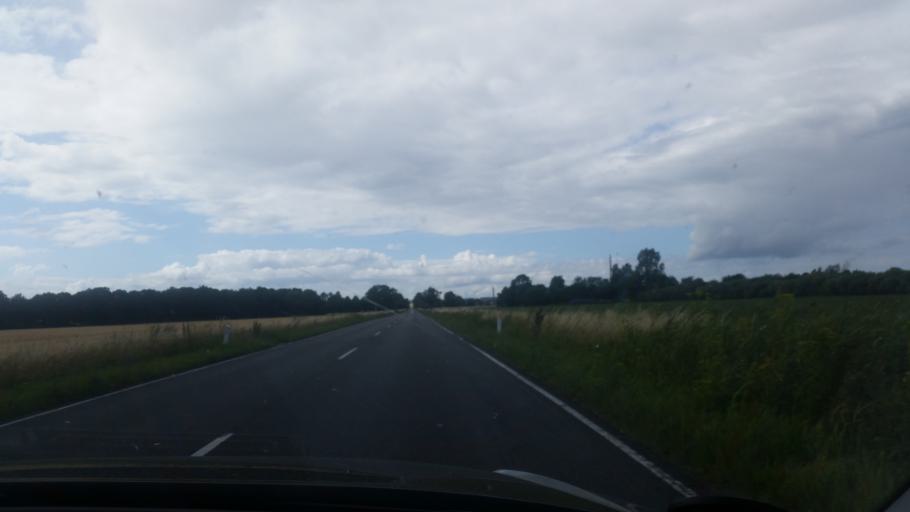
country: DK
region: Zealand
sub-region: Odsherred Kommune
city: Horve
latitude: 55.7732
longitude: 11.4881
